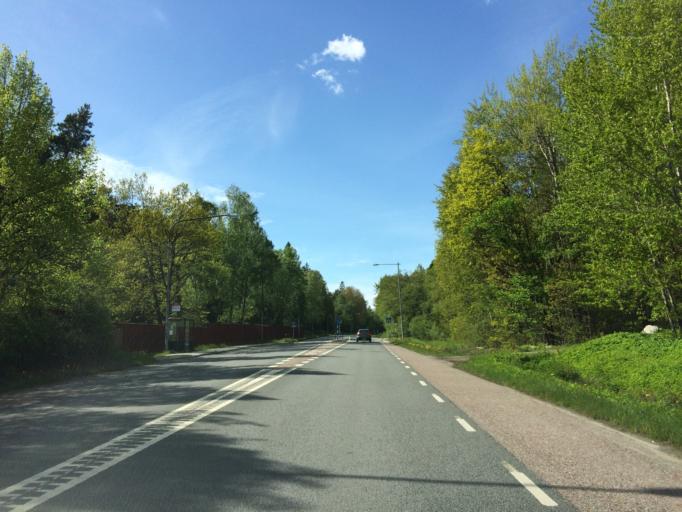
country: SE
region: Stockholm
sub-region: Norrtalje Kommun
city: Bergshamra
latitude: 59.4160
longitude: 18.0144
